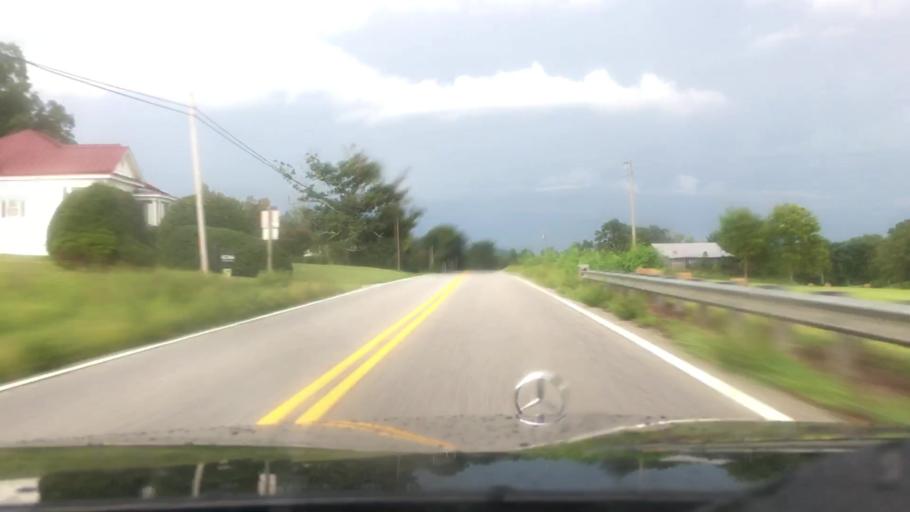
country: US
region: Virginia
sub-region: Nelson County
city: Lovingston
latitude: 37.7717
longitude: -78.9812
